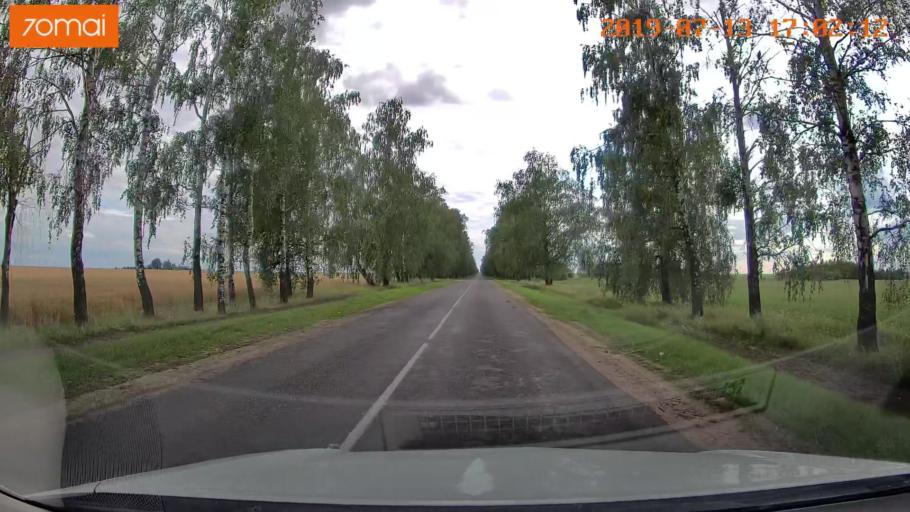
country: BY
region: Mogilev
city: Kirawsk
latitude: 53.2883
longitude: 29.3893
